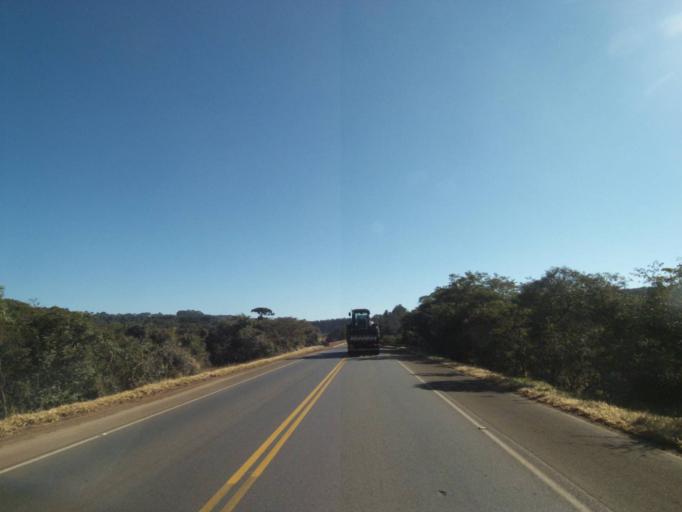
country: BR
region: Parana
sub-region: Tibagi
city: Tibagi
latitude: -24.4812
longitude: -50.4430
